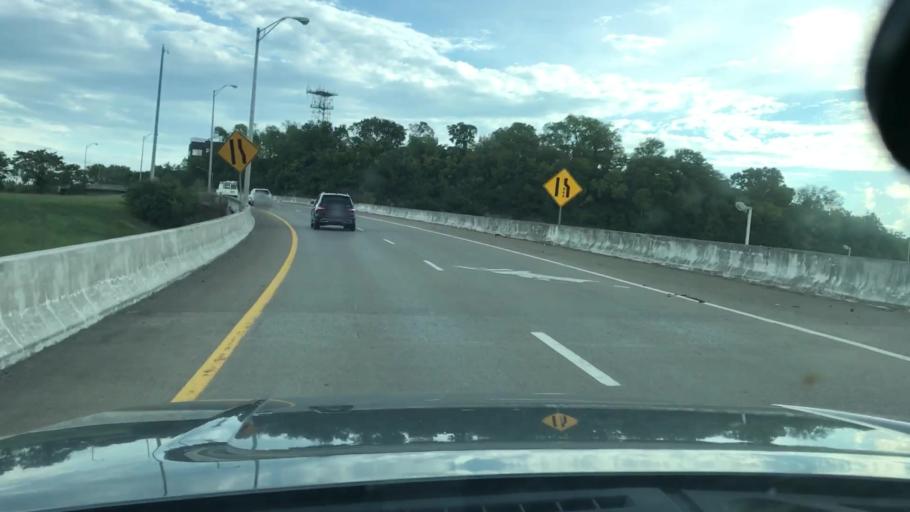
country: US
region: Tennessee
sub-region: Davidson County
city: Nashville
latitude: 36.1472
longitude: -86.7811
